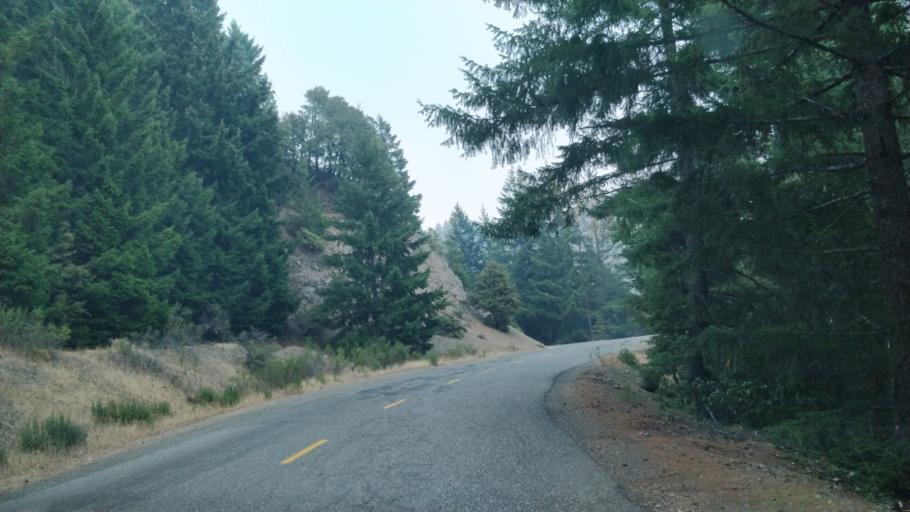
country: US
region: California
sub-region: Humboldt County
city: Rio Dell
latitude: 40.2732
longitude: -124.0791
